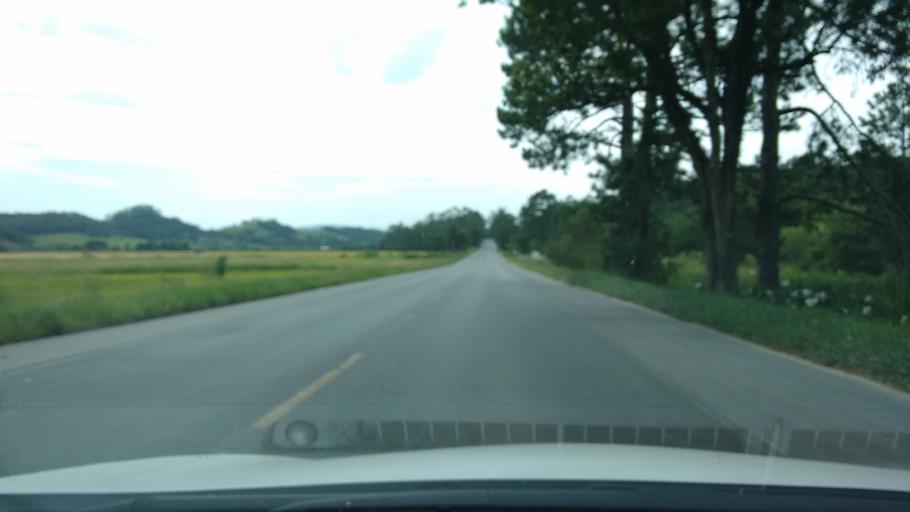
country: BR
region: Santa Catarina
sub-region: Otacilio Costa
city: Otacilio Costa
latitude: -27.2529
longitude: -50.0262
